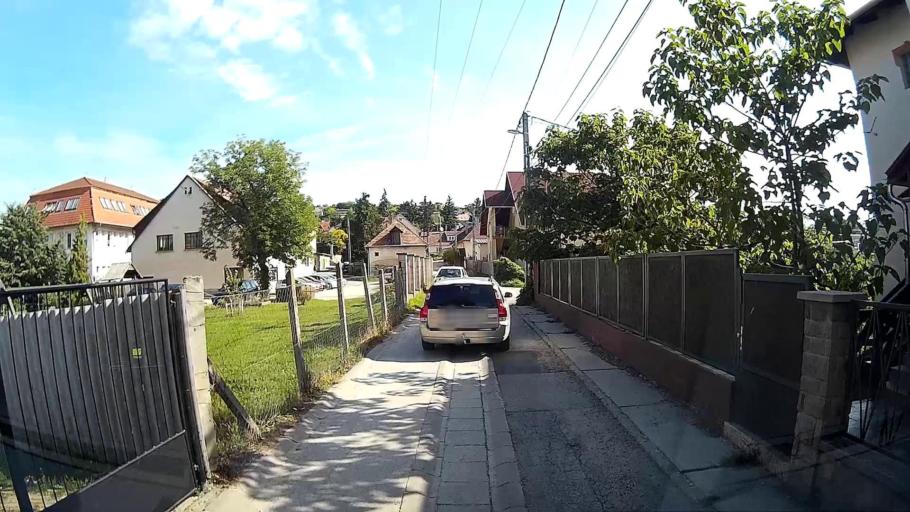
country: HU
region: Pest
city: Nagykovacsi
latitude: 47.6483
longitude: 19.0118
